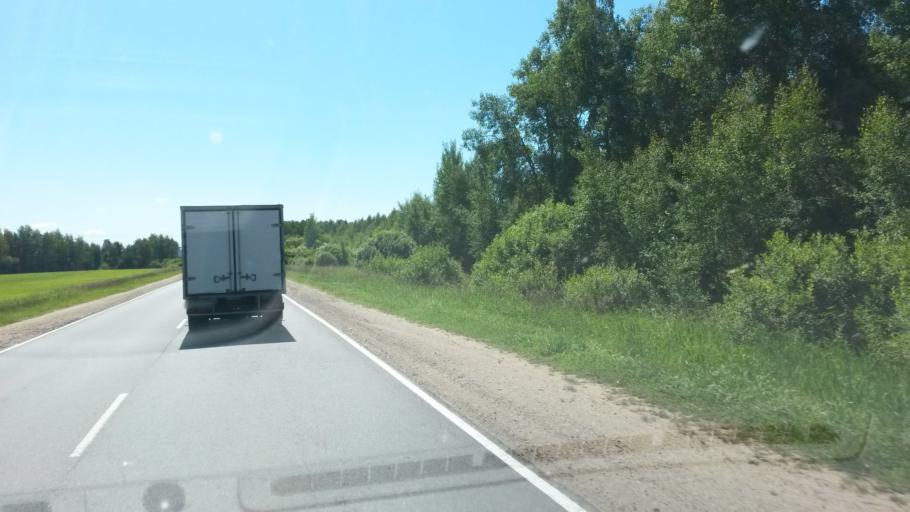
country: RU
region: Ivanovo
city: Novo-Talitsy
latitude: 57.0348
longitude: 40.7477
